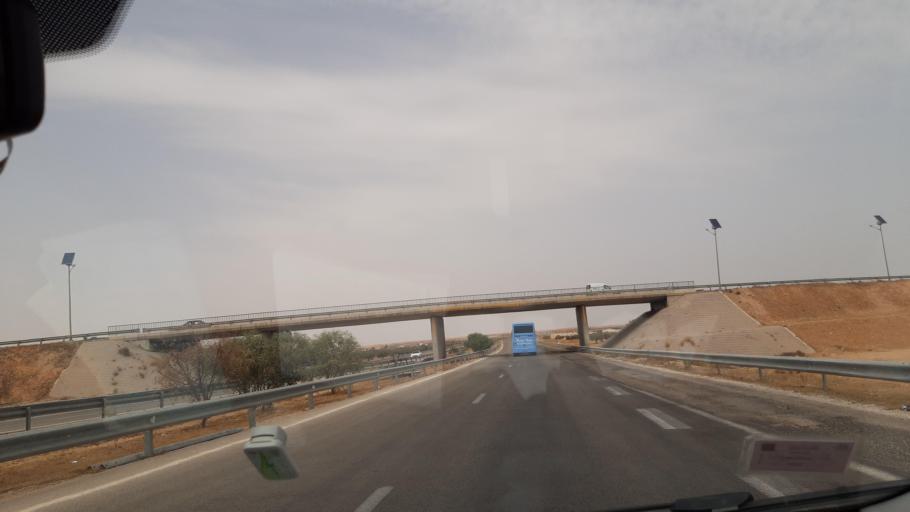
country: TN
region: Safaqis
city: Sfax
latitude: 34.7313
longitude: 10.5913
